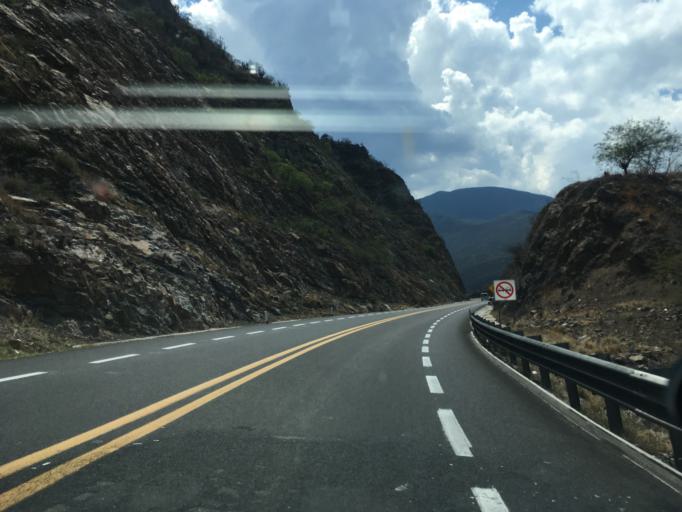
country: MX
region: Puebla
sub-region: San Jose Miahuatlan
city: San Pedro Tetitlan
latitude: 18.1526
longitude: -97.3003
